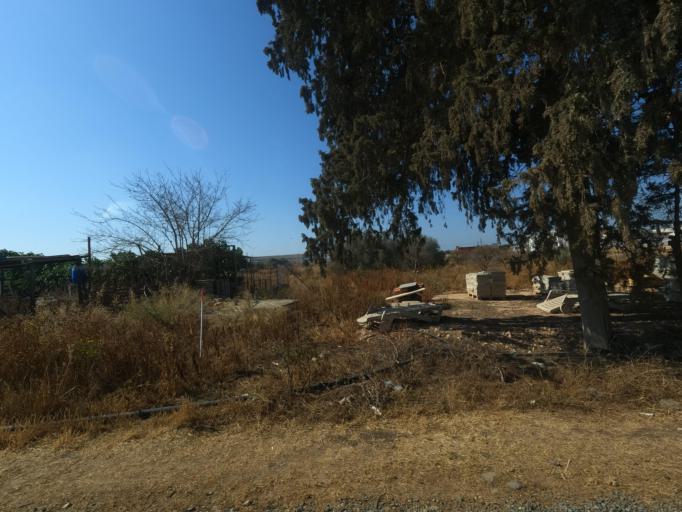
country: CY
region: Ammochostos
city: Frenaros
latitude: 35.0410
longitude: 33.9307
